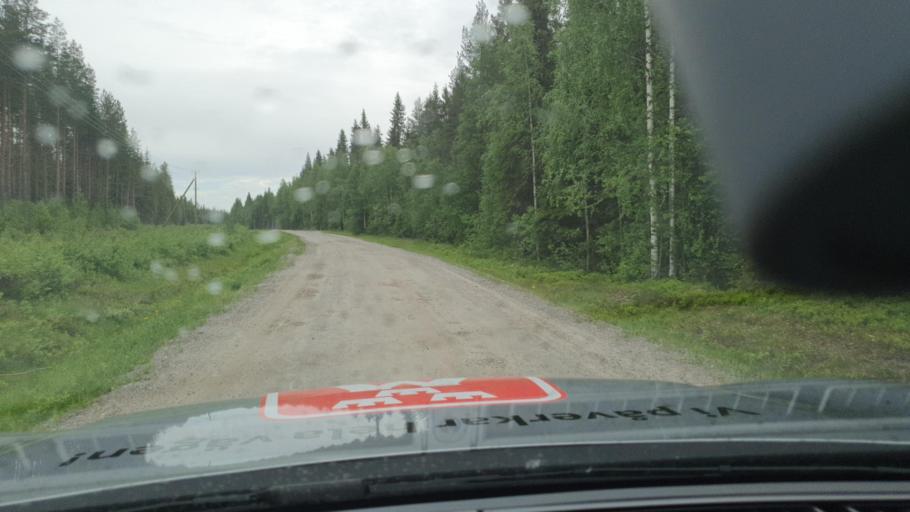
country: SE
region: Norrbotten
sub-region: Kalix Kommun
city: Rolfs
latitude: 66.0400
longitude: 23.0539
